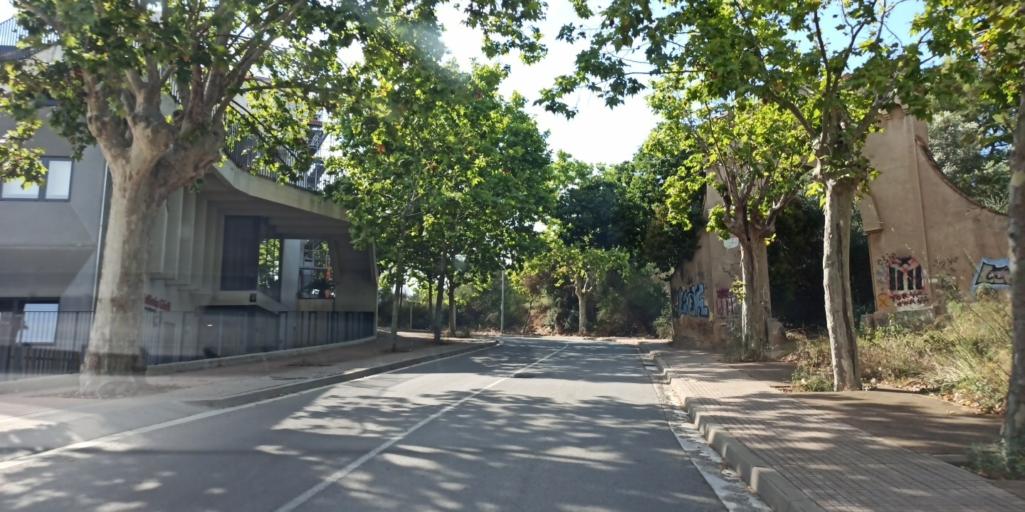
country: ES
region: Catalonia
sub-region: Provincia de Barcelona
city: Santa Coloma de Cervello
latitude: 41.3647
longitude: 2.0291
